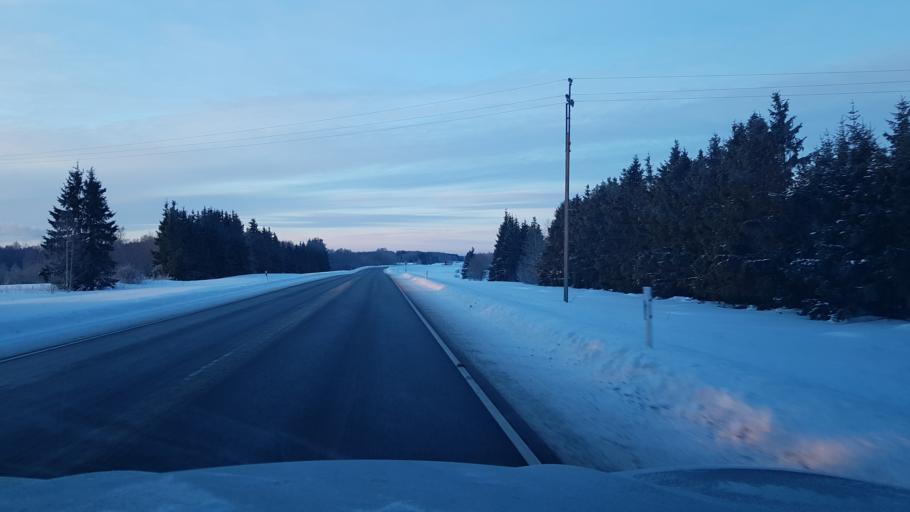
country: EE
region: Ida-Virumaa
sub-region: Narva-Joesuu linn
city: Narva-Joesuu
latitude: 59.3878
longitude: 27.9757
